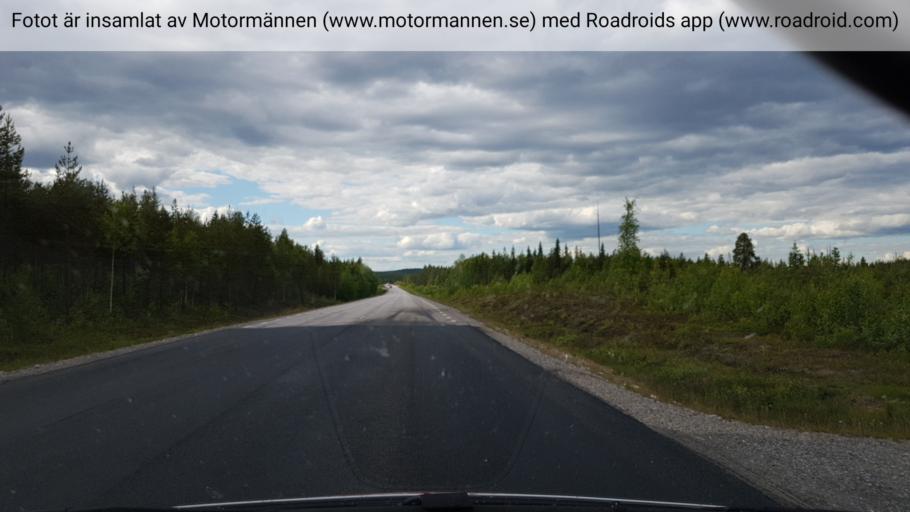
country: SE
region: Norrbotten
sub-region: Overkalix Kommun
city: OEverkalix
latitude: 66.6238
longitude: 22.2245
